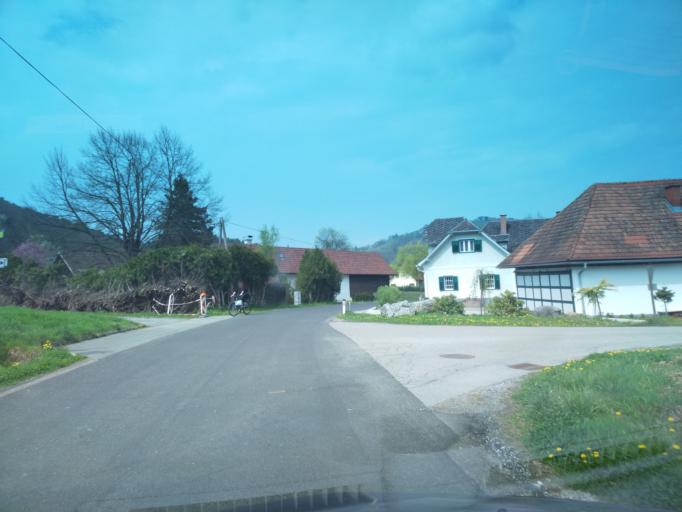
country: AT
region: Styria
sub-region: Politischer Bezirk Leibnitz
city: Kitzeck im Sausal
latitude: 46.7486
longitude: 15.4194
